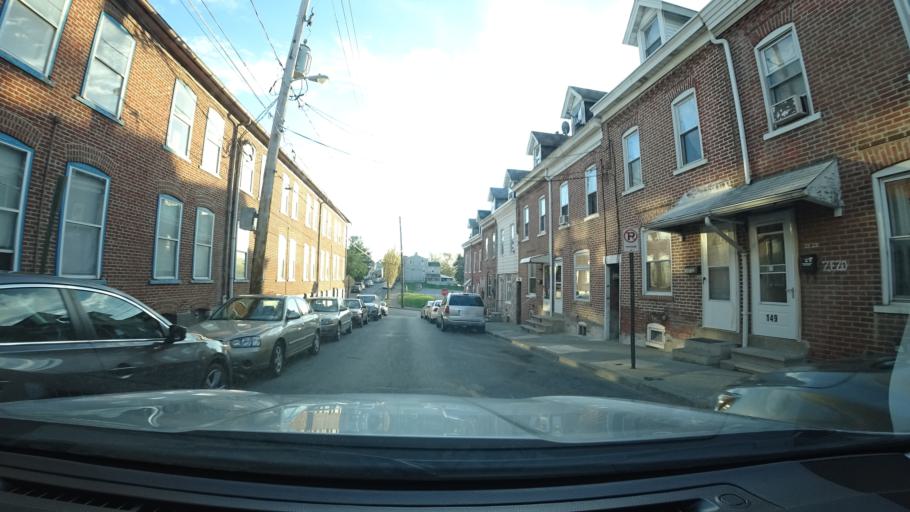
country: US
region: Pennsylvania
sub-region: Lehigh County
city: Fullerton
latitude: 40.6167
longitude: -75.4623
